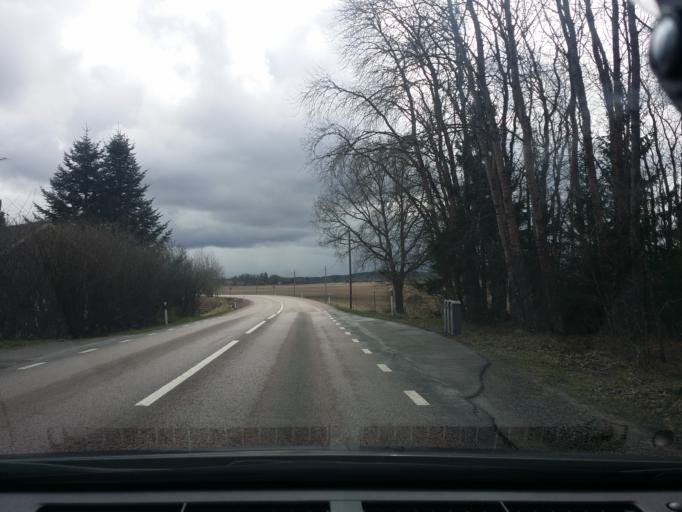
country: SE
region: Uppsala
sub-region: Enkopings Kommun
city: Irsta
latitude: 59.7833
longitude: 16.8409
